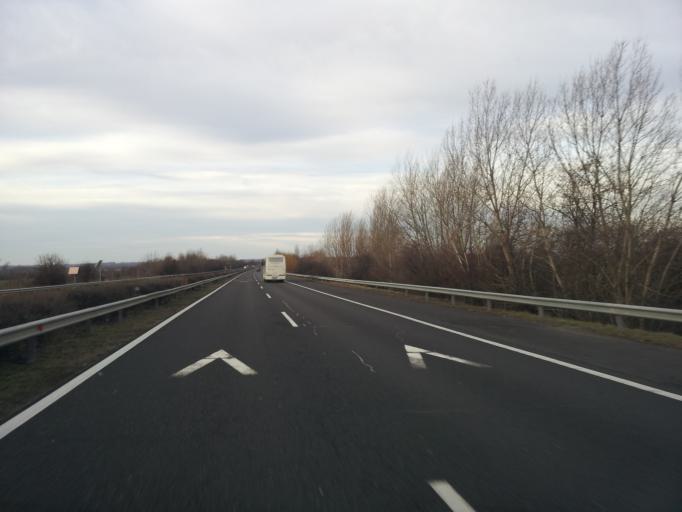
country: HU
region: Fejer
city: Lepseny
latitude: 47.0113
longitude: 18.2372
